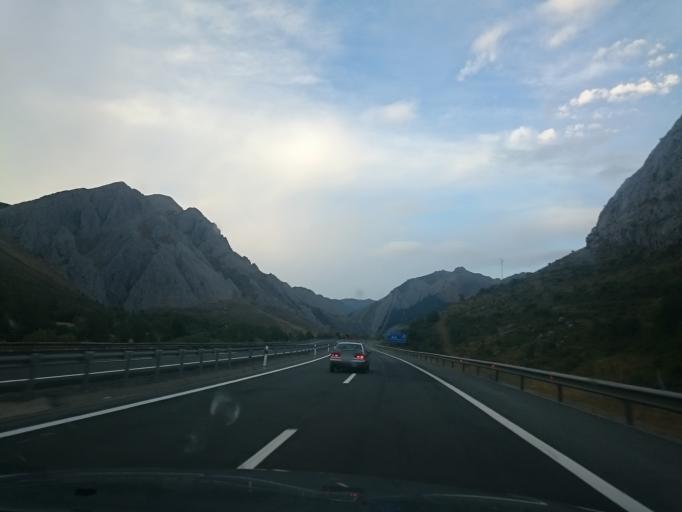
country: ES
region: Castille and Leon
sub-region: Provincia de Leon
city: Sena de Luna
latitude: 42.9221
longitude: -5.8746
